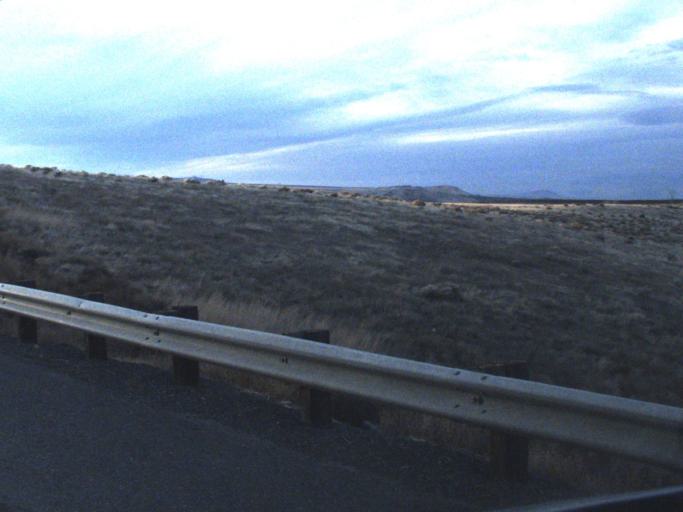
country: US
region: Washington
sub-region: Benton County
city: Finley
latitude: 46.0534
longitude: -118.8674
